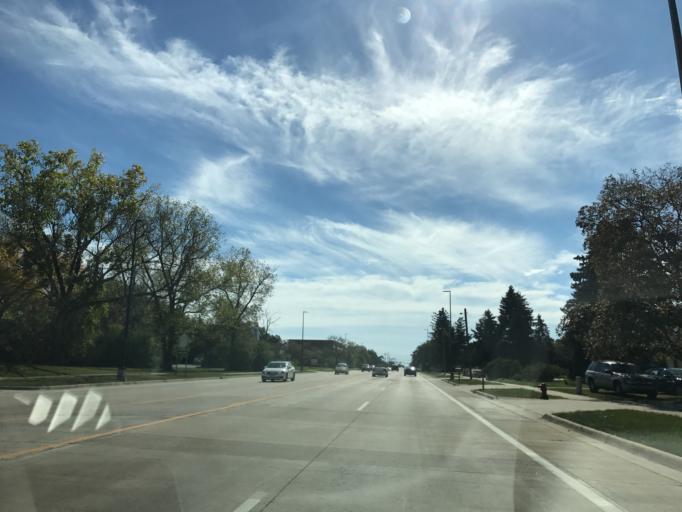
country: US
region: Michigan
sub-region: Washtenaw County
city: Ann Arbor
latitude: 42.2512
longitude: -83.6807
